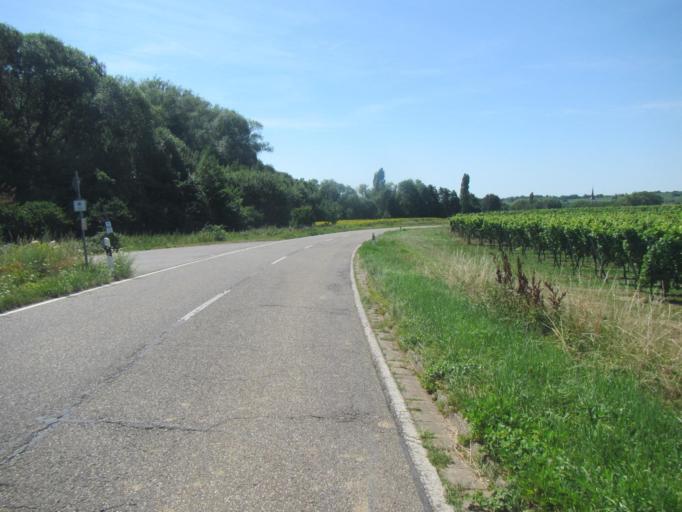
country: DE
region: Rheinland-Pfalz
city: Gocklingen
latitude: 49.1695
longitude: 8.0430
